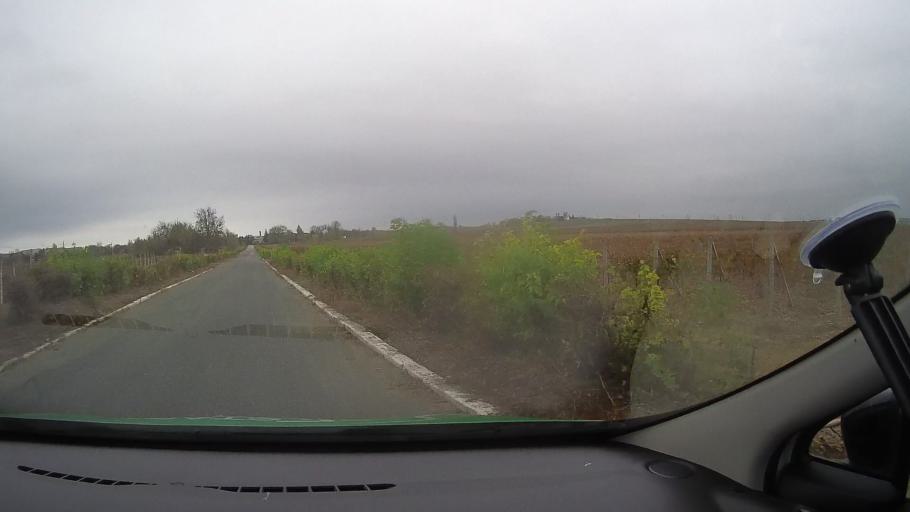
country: RO
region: Constanta
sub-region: Oras Murfatlar
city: Murfatlar
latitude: 44.1721
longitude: 28.4225
